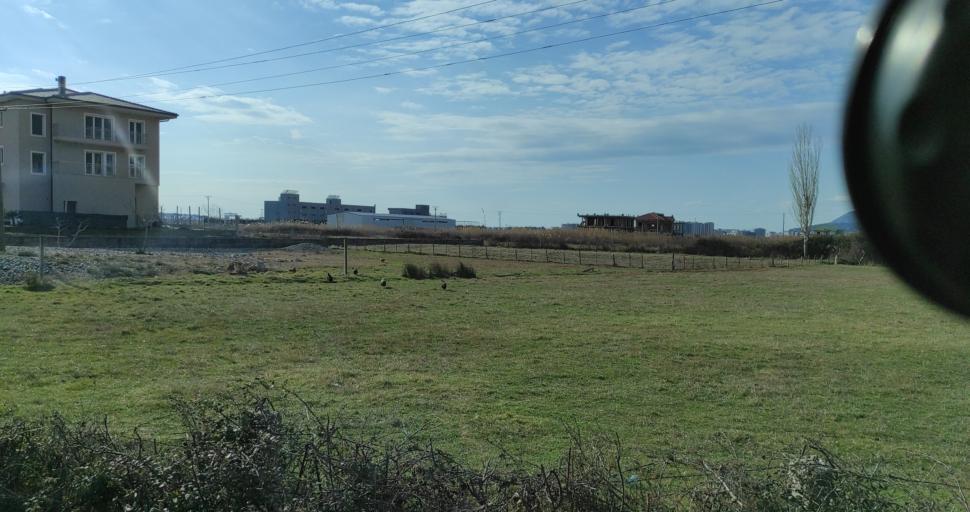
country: AL
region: Lezhe
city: Lezhe
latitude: 41.7864
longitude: 19.6279
